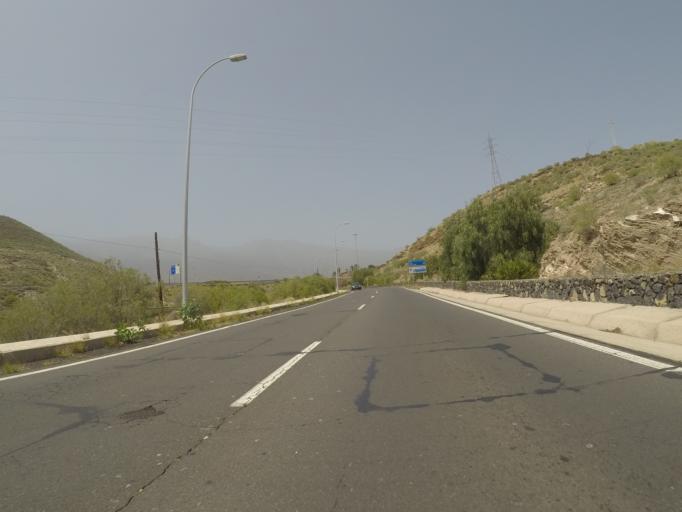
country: ES
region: Canary Islands
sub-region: Provincia de Santa Cruz de Tenerife
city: Guimar
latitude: 28.3032
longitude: -16.3811
